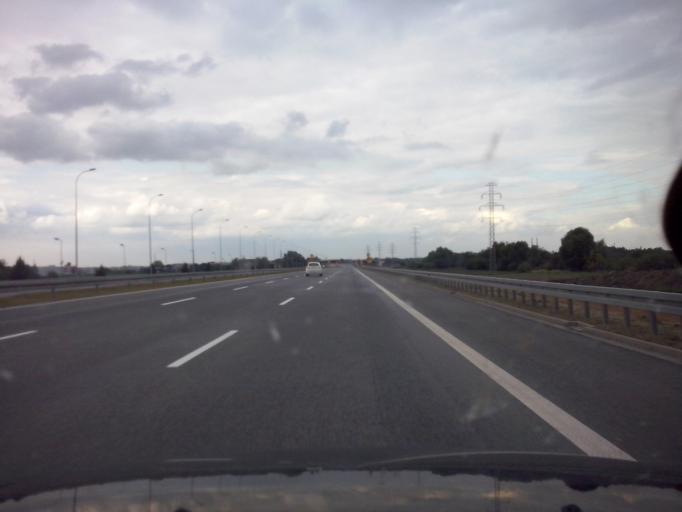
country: PL
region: Lesser Poland Voivodeship
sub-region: Powiat wielicki
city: Kokotow
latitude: 50.0237
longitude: 20.0625
